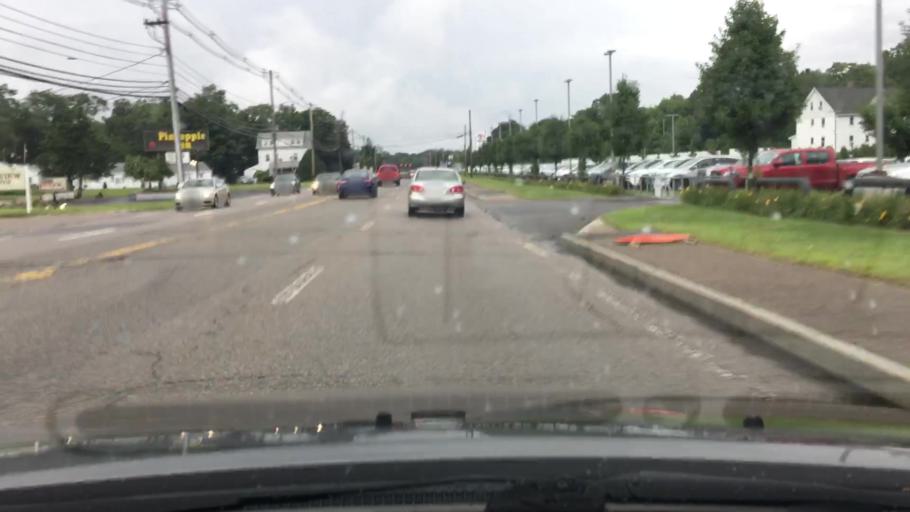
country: US
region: Massachusetts
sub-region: Norfolk County
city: Plainville
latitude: 41.9608
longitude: -71.3411
